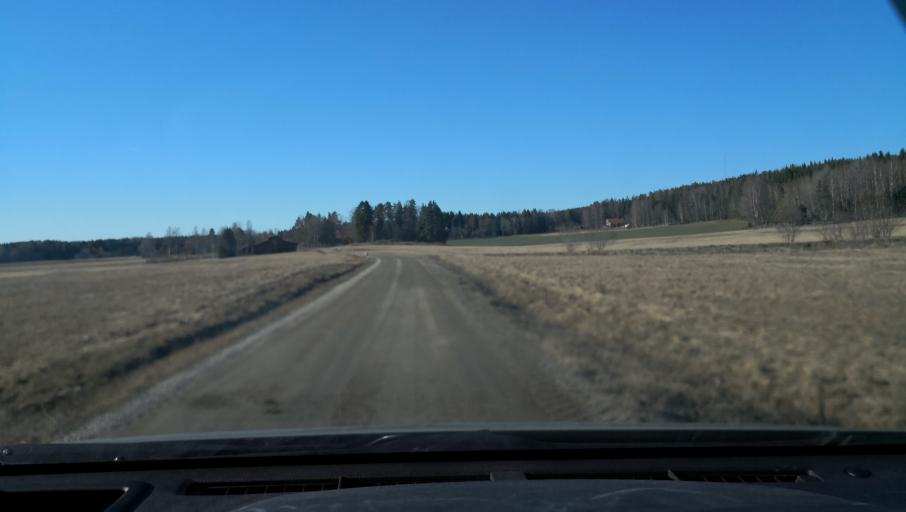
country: SE
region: Vaestmanland
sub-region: Sala Kommun
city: Sala
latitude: 60.1485
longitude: 16.6408
